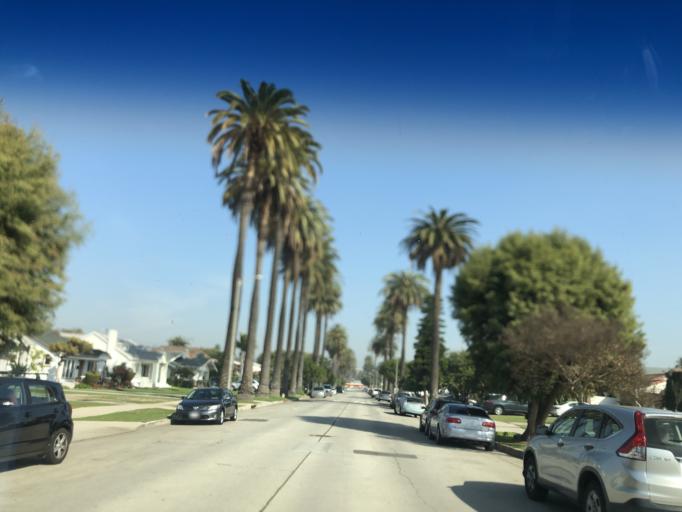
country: US
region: California
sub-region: Los Angeles County
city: Hollywood
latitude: 34.0517
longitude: -118.3275
